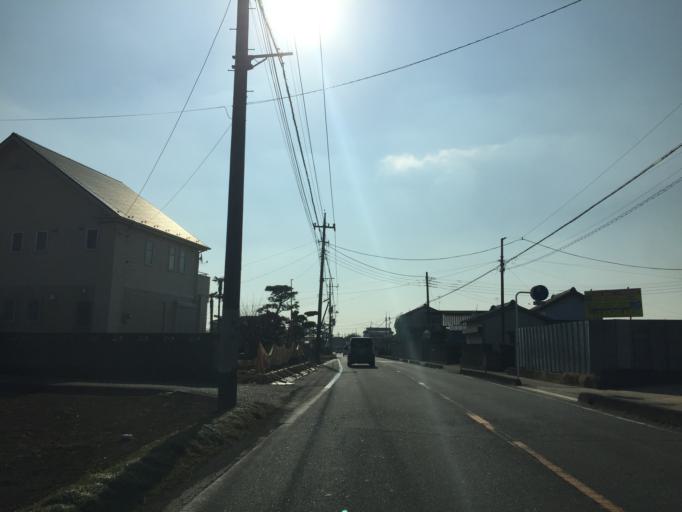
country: JP
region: Saitama
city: Oi
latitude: 35.8646
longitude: 139.5565
